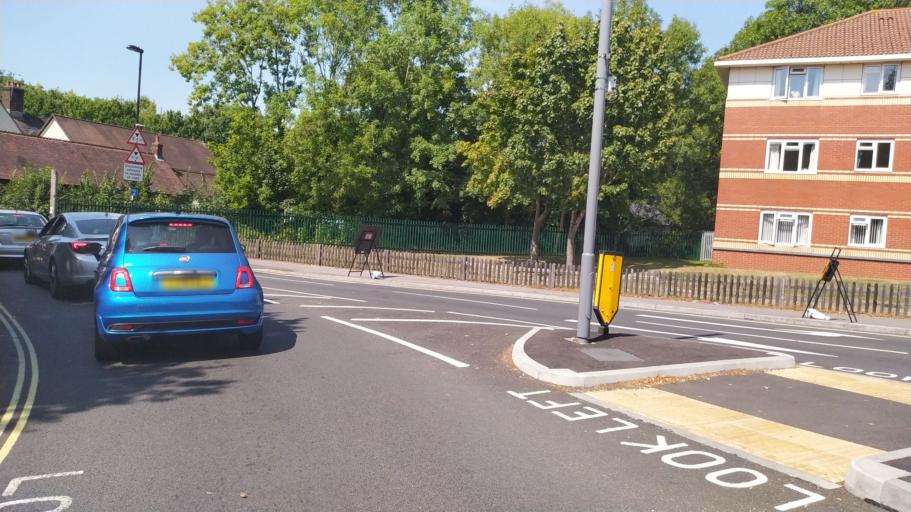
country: GB
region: England
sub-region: Hampshire
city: Eastleigh
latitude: 50.9420
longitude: -1.3738
